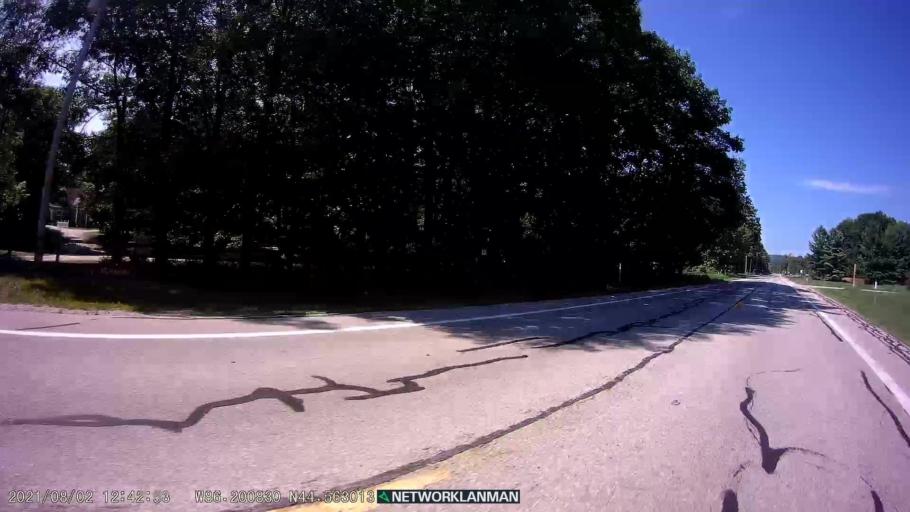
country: US
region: Michigan
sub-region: Benzie County
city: Frankfort
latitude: 44.5634
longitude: -86.2008
